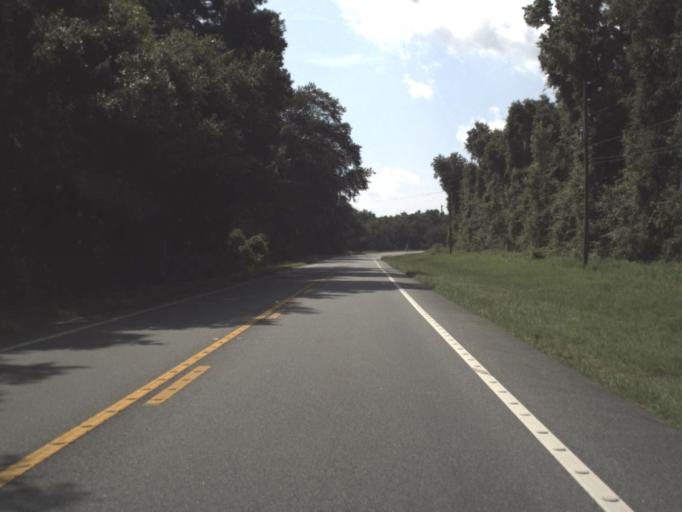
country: US
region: Florida
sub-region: Citrus County
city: Hernando
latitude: 28.9125
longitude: -82.3825
